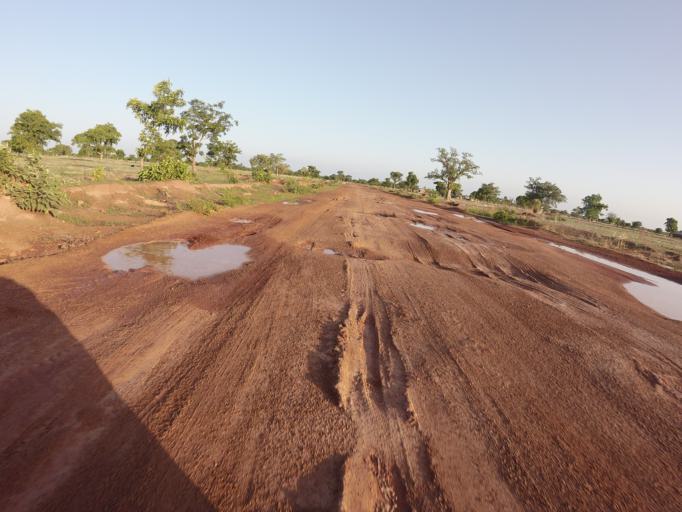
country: TG
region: Savanes
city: Sansanne-Mango
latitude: 10.2925
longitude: -0.0874
